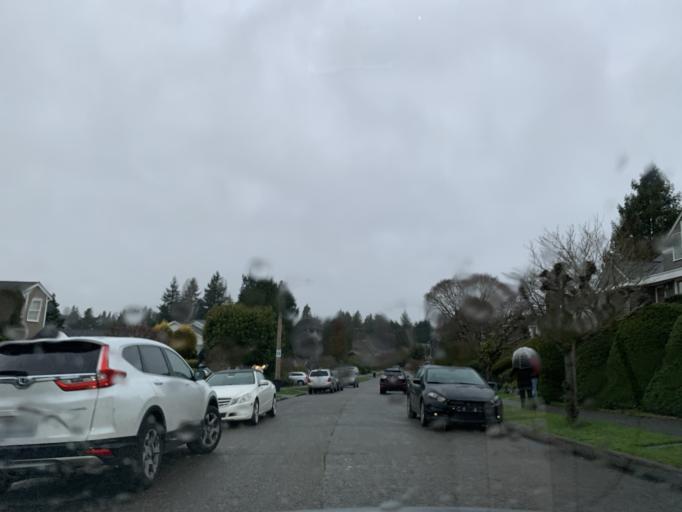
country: US
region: Washington
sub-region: King County
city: Yarrow Point
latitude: 47.6709
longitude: -122.2772
